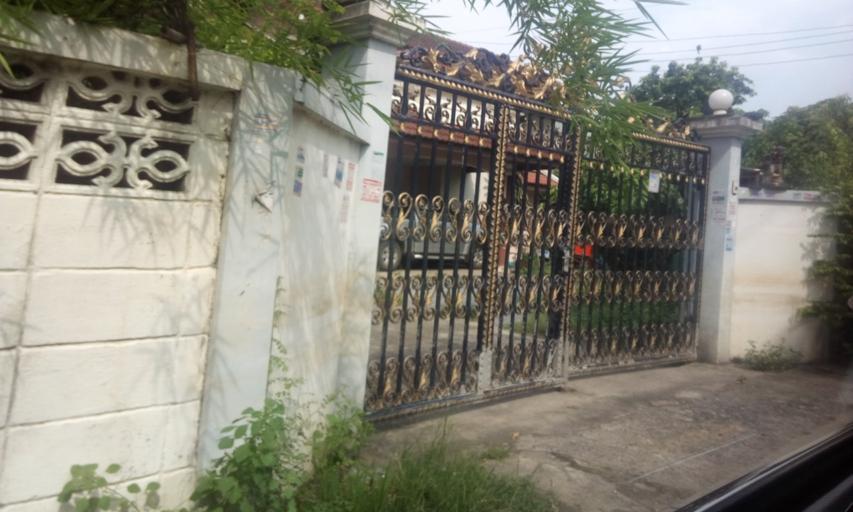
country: TH
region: Bangkok
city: Sai Mai
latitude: 13.9819
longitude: 100.6235
